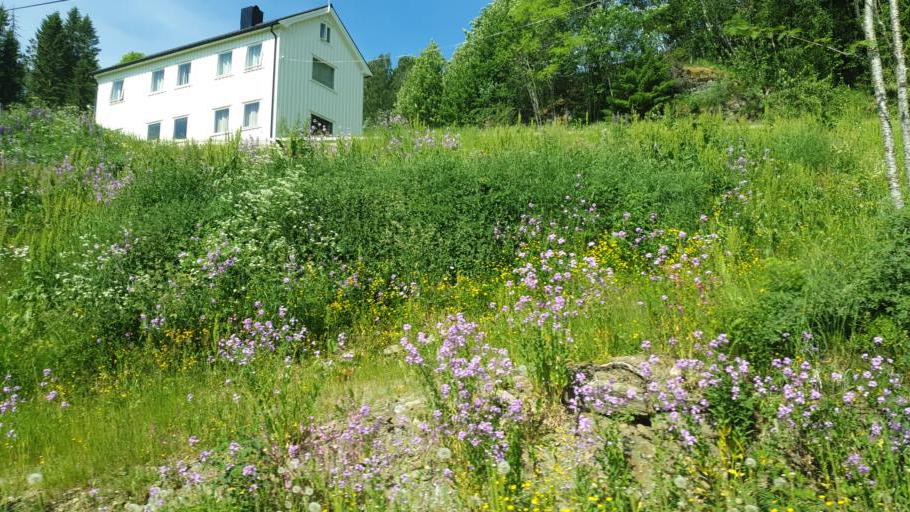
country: NO
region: Nord-Trondelag
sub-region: Leksvik
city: Leksvik
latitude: 63.6891
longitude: 10.6748
